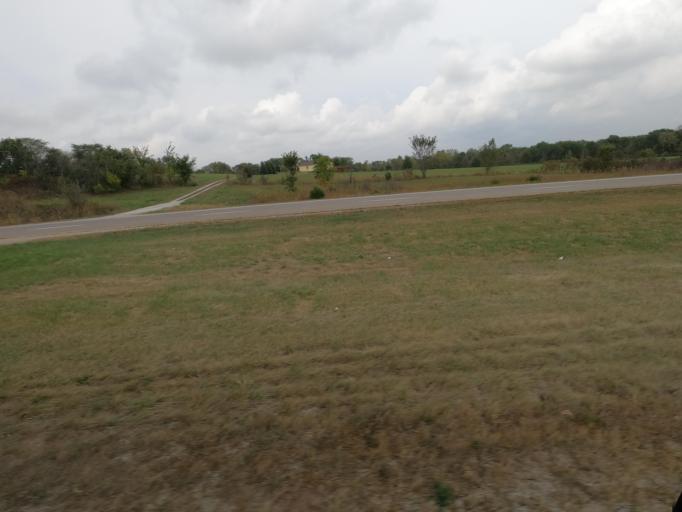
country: US
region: Iowa
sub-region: Wapello County
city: Ottumwa
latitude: 41.0960
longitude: -92.5040
